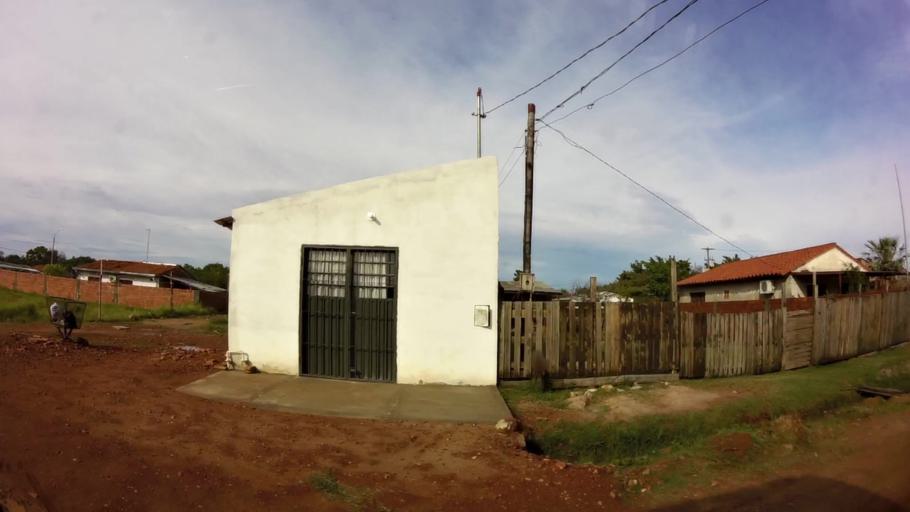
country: PY
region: Central
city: Limpio
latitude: -25.1839
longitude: -57.4826
